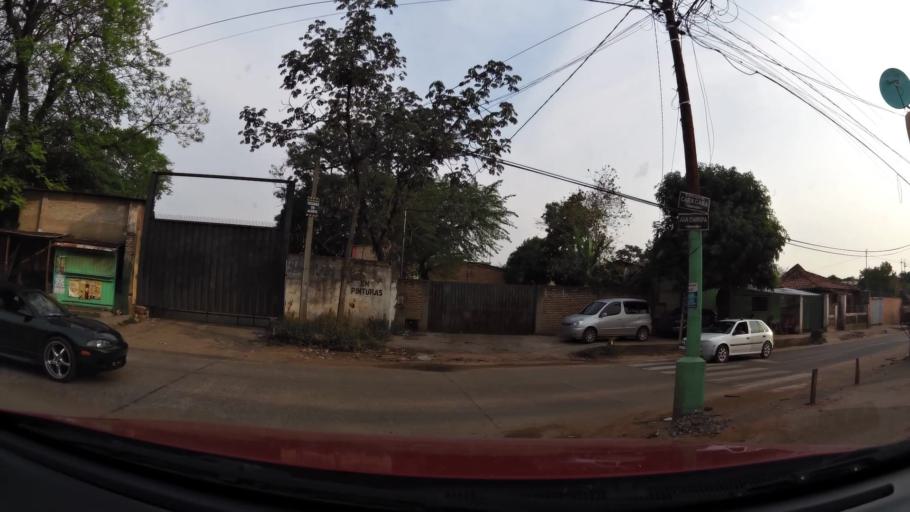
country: PY
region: Central
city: Lambare
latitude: -25.3319
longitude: -57.5768
